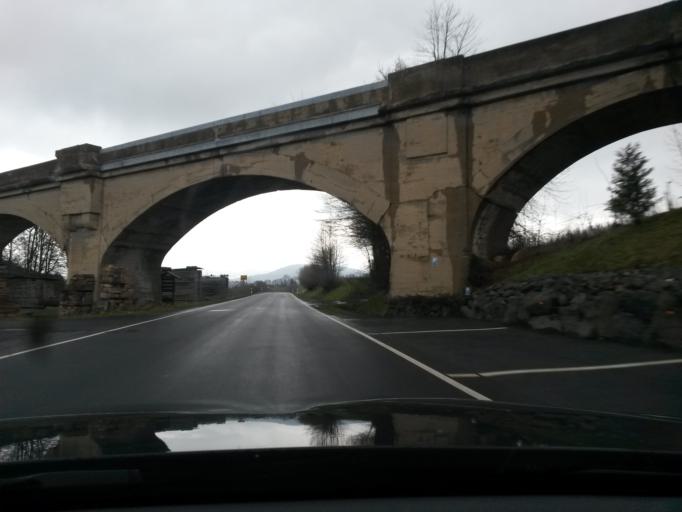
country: DE
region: Hesse
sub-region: Regierungsbezirk Kassel
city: Hilders
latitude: 50.5447
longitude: 10.0147
